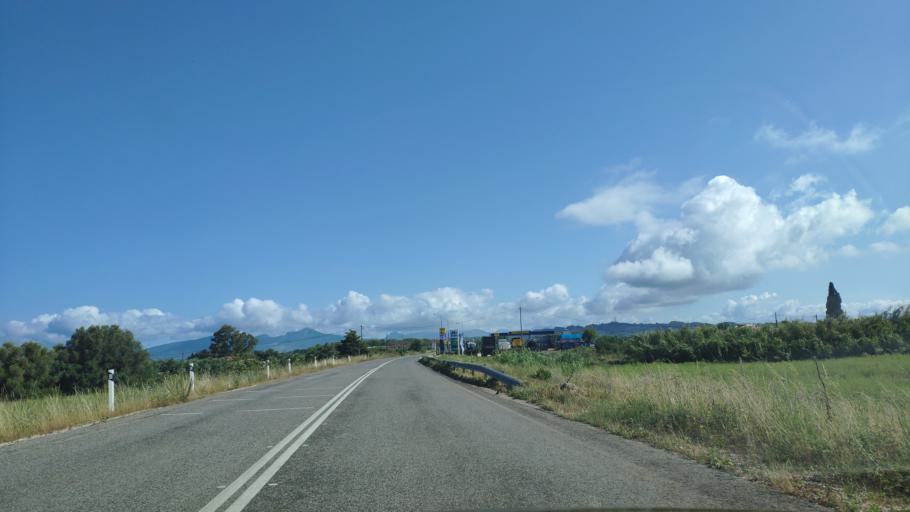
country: GR
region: Epirus
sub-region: Nomos Prevezis
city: Preveza
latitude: 38.9902
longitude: 20.7136
